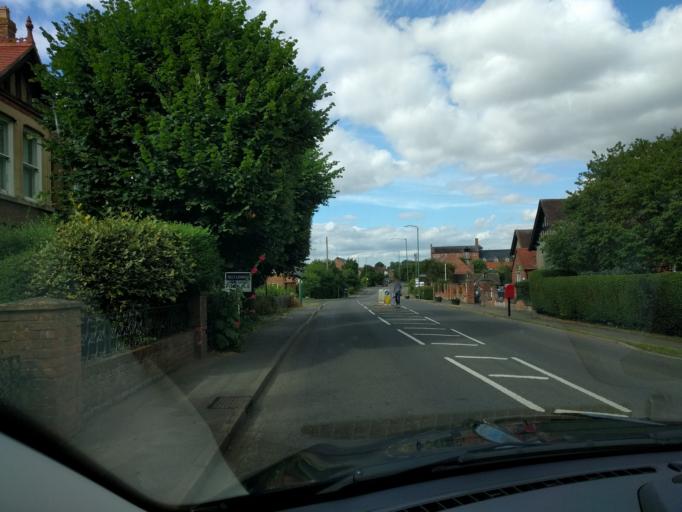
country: GB
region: England
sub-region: Warwickshire
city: Shipston on Stour
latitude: 52.0665
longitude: -1.6234
